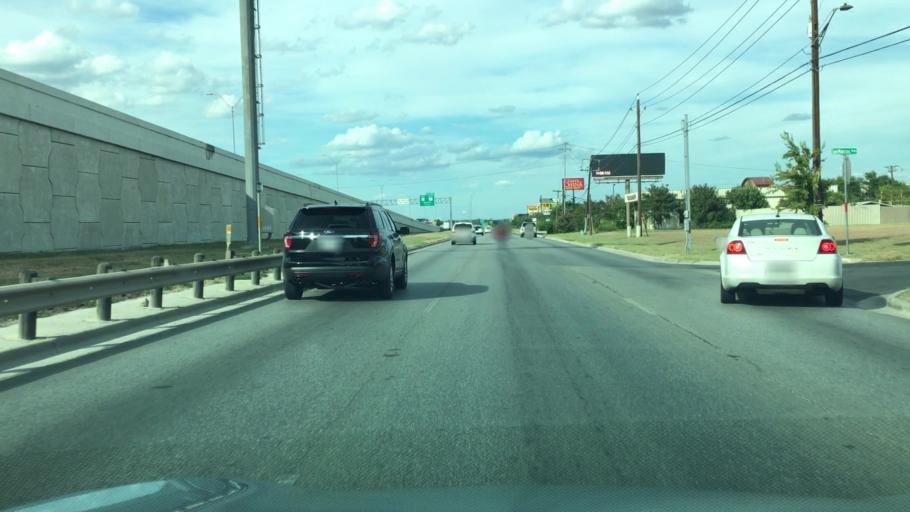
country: US
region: Texas
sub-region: Hays County
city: San Marcos
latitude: 29.8584
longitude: -97.9510
